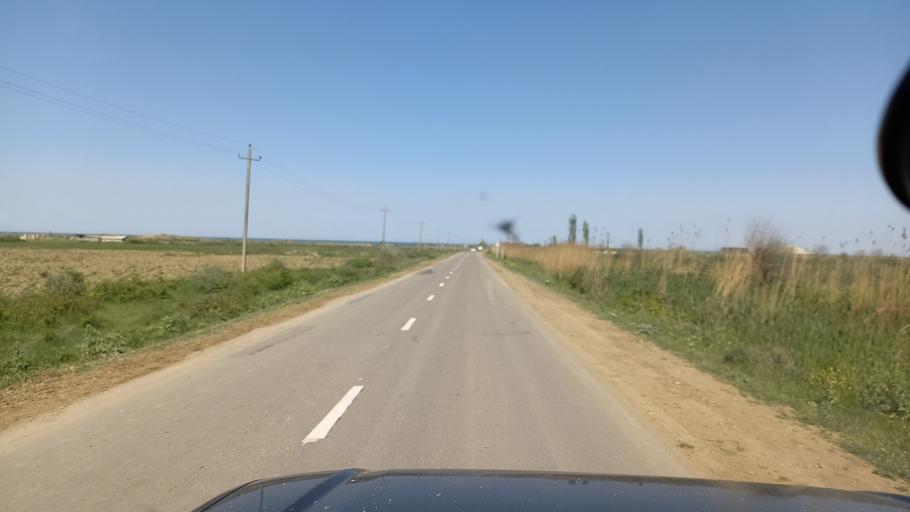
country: RU
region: Dagestan
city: Khazar
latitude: 41.9458
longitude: 48.3480
